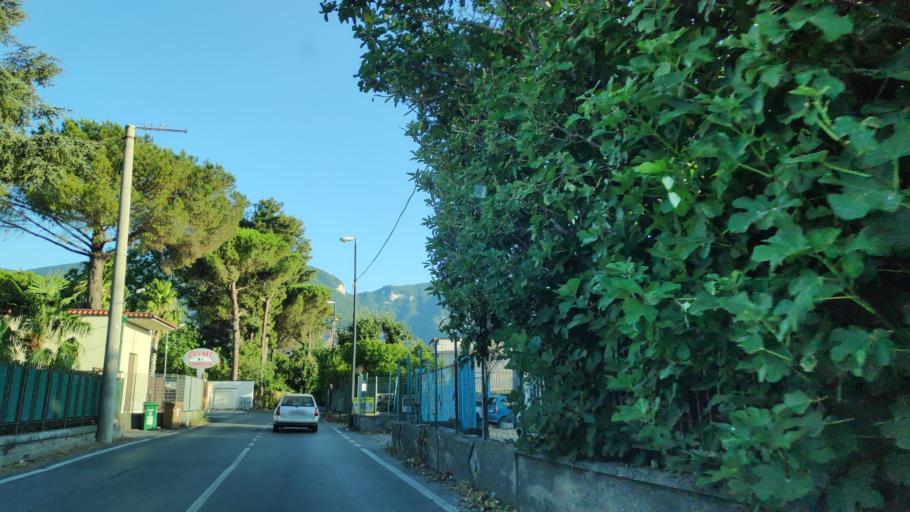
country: IT
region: Campania
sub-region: Provincia di Salerno
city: Pagani
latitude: 40.7549
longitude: 14.6158
